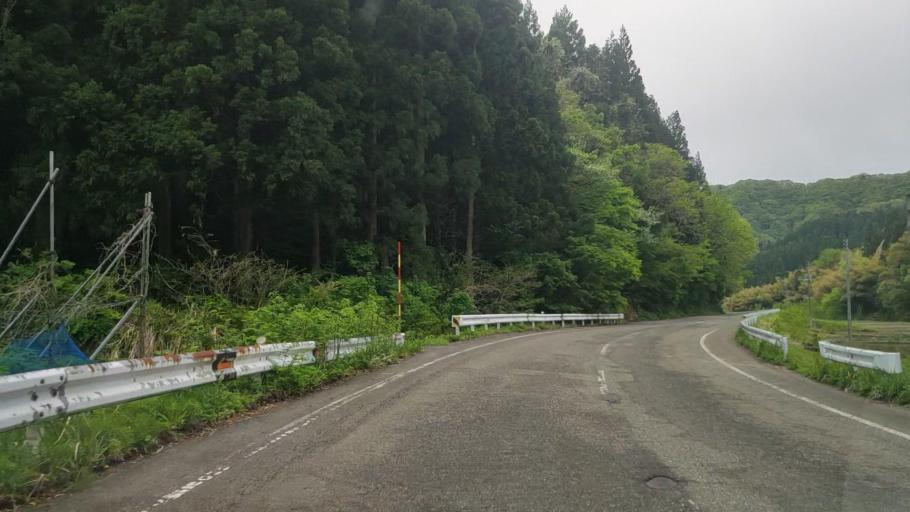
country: JP
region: Niigata
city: Gosen
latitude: 37.7129
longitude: 139.1103
